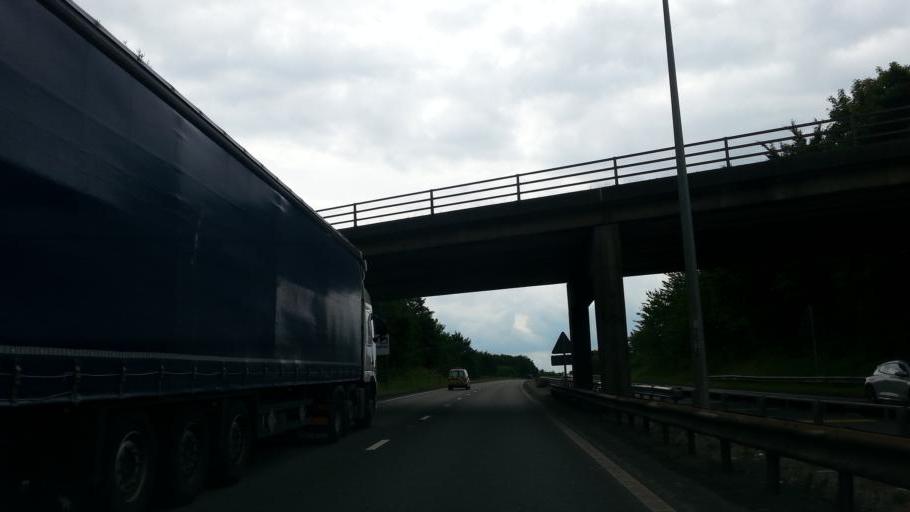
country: GB
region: England
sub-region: Warwickshire
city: Curdworth
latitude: 52.5636
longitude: -1.7701
